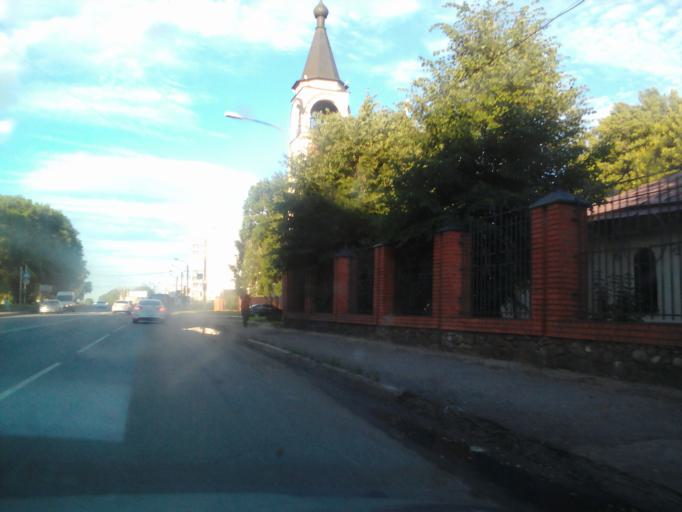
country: RU
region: Kursk
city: Kurchatov
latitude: 51.6546
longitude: 35.6930
